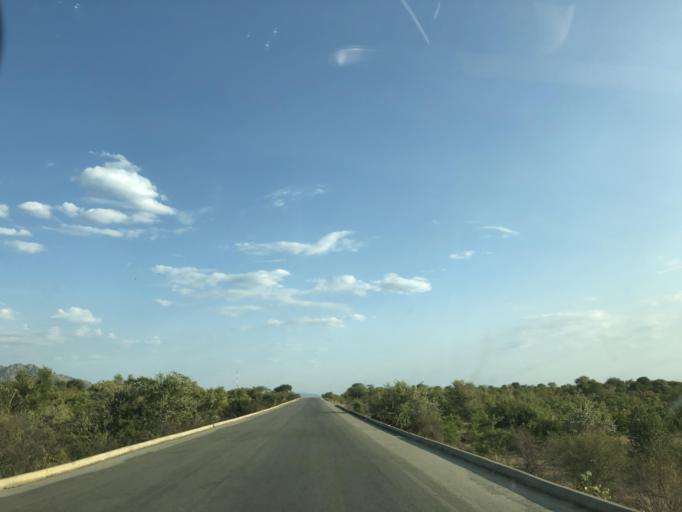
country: AO
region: Huila
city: Caluquembe
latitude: -13.5074
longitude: 13.9184
